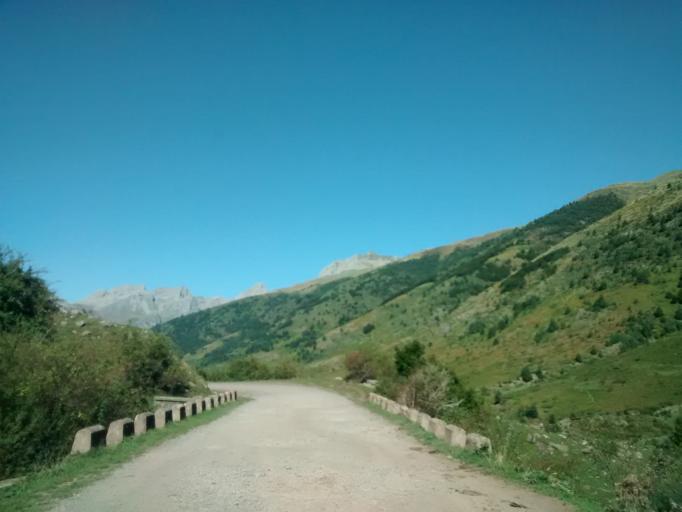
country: ES
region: Aragon
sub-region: Provincia de Huesca
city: Aragues del Puerto
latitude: 42.8457
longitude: -0.6629
